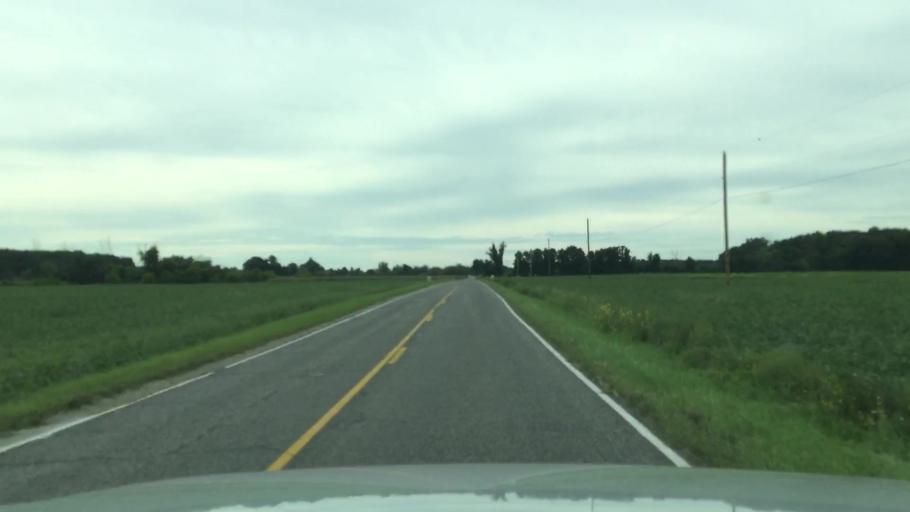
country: US
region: Michigan
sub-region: Genesee County
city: Flushing
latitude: 43.0707
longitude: -83.9876
